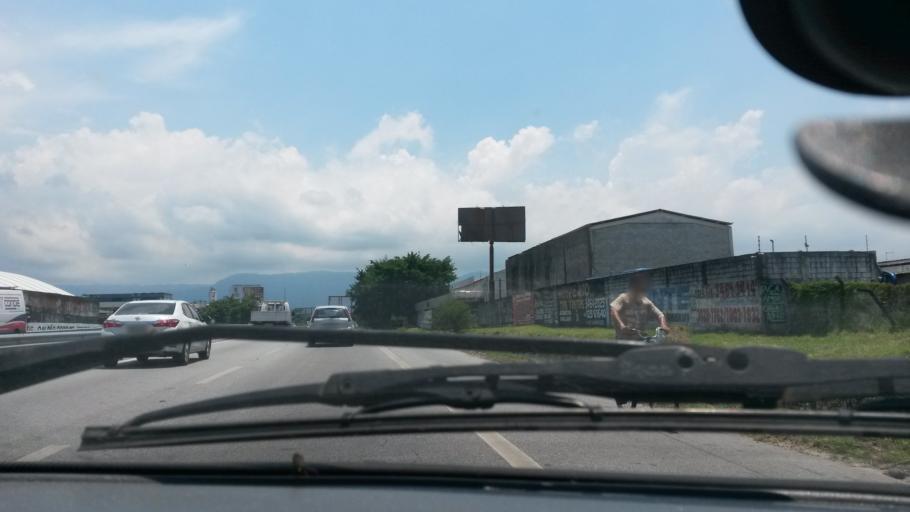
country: BR
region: Sao Paulo
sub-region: Sao Vicente
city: Sao Vicente
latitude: -23.9497
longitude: -46.4136
